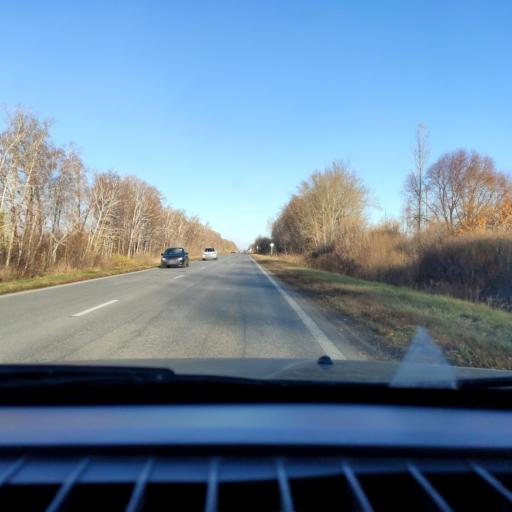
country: RU
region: Samara
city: Tol'yatti
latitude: 53.6128
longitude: 49.3148
